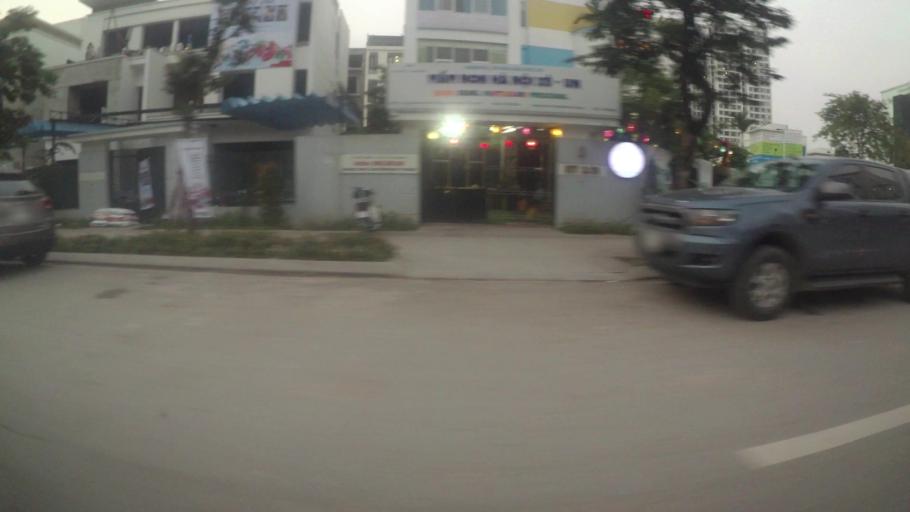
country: VN
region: Ha Noi
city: Tay Ho
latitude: 21.0674
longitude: 105.7964
